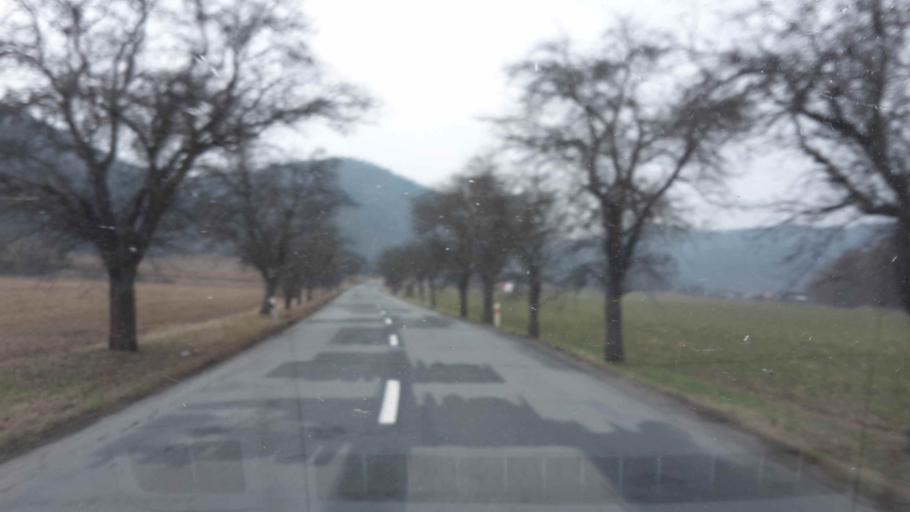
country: CZ
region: South Moravian
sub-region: Okres Brno-Venkov
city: Dolni Loucky
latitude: 49.3905
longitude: 16.3724
